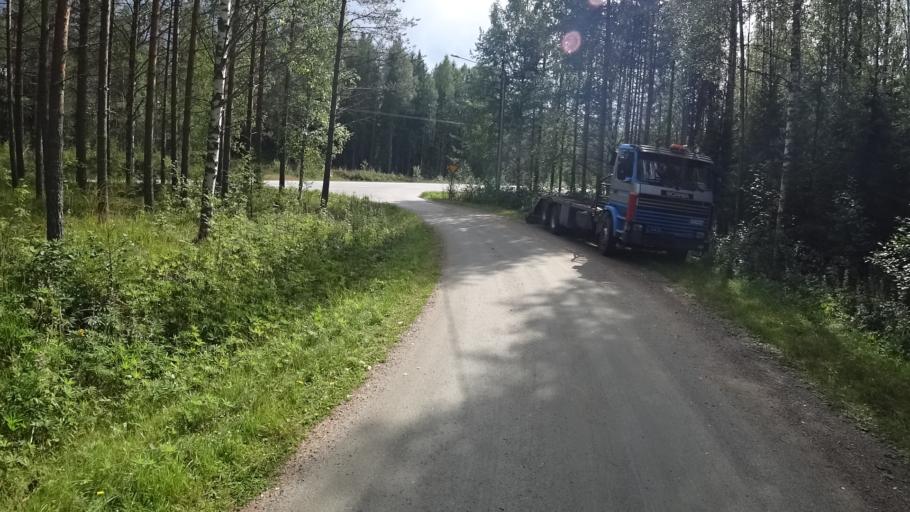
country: FI
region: North Karelia
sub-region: Joensuu
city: Ilomantsi
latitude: 62.6322
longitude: 31.2759
